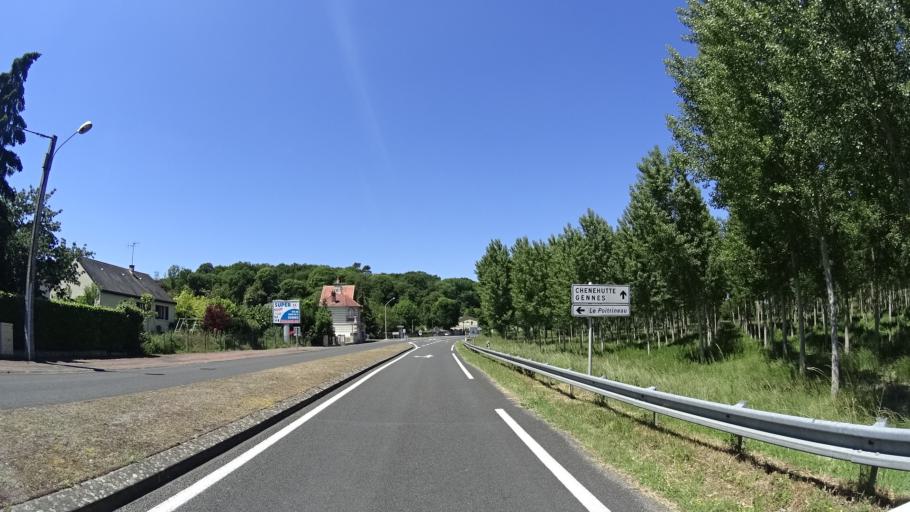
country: FR
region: Pays de la Loire
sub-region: Departement de Maine-et-Loire
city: Saumur
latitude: 47.2794
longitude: -0.1189
